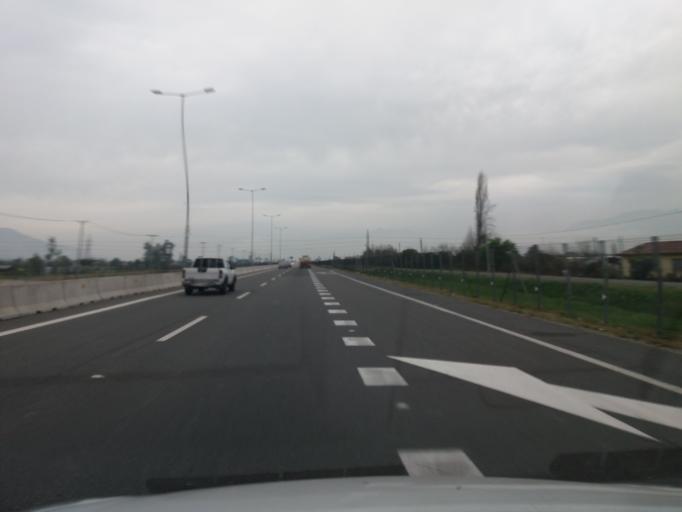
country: CL
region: Valparaiso
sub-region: Provincia de Quillota
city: Quillota
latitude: -32.9246
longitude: -71.2813
